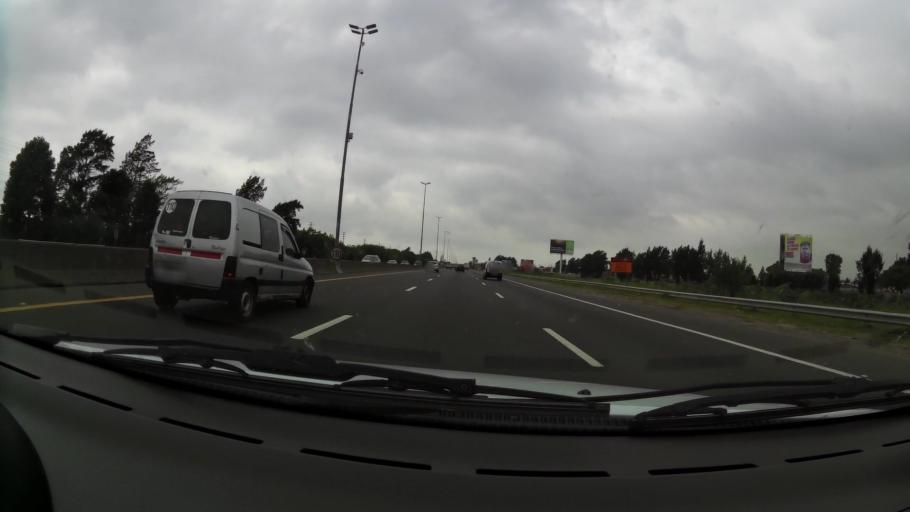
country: AR
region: Buenos Aires
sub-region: Partido de Avellaneda
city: Avellaneda
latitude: -34.6827
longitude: -58.3107
